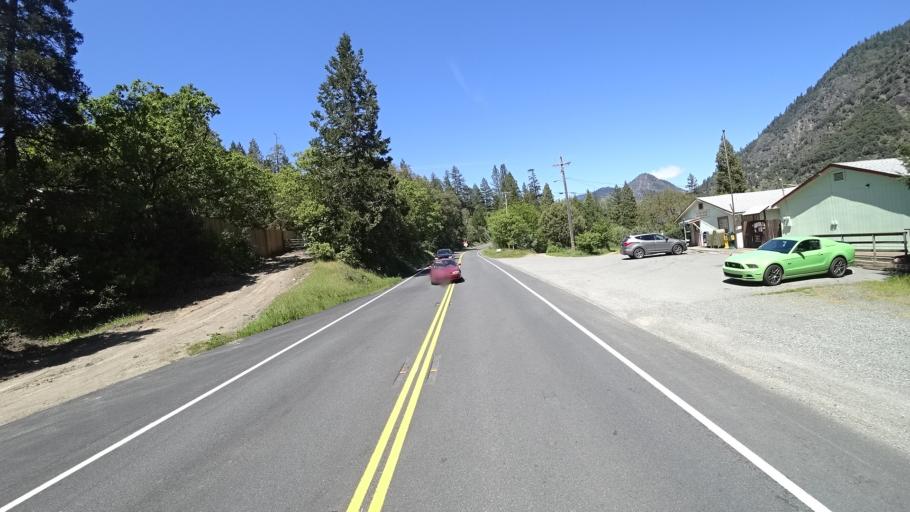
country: US
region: California
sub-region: Humboldt County
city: Willow Creek
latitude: 40.8223
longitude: -123.4836
